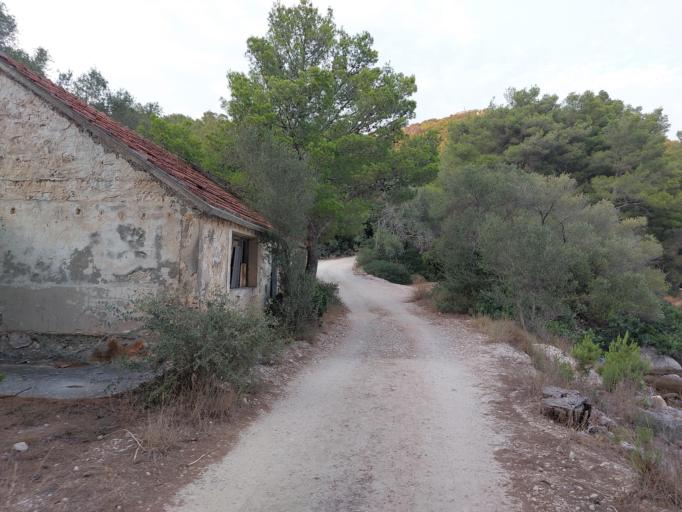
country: HR
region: Dubrovacko-Neretvanska
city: Smokvica
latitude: 42.7660
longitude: 16.8116
